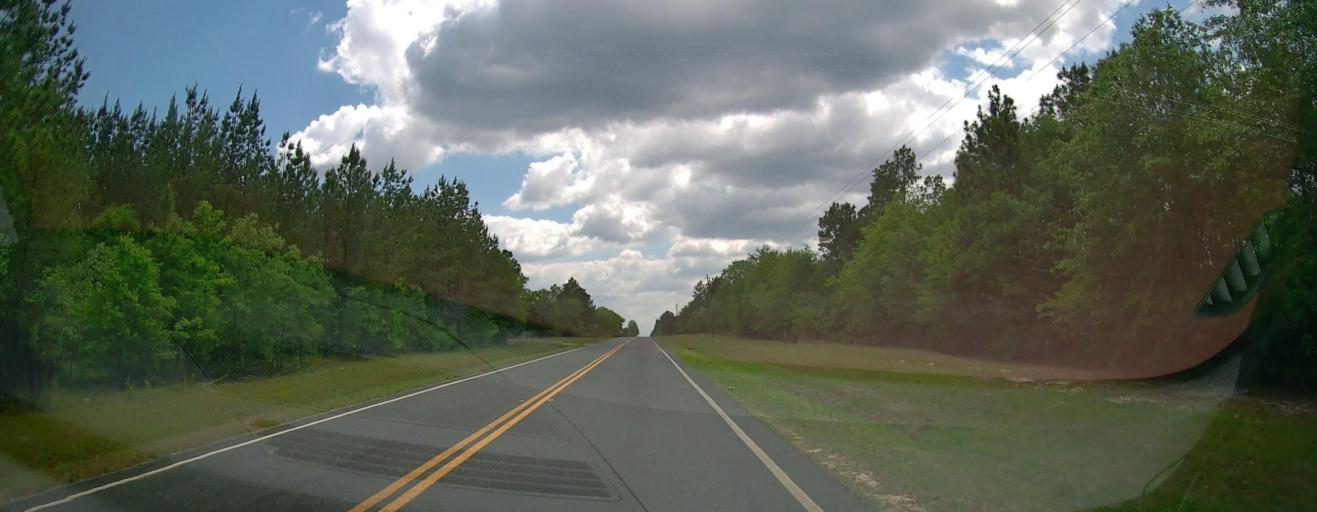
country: US
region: Georgia
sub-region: Treutlen County
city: Soperton
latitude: 32.4749
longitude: -82.6014
